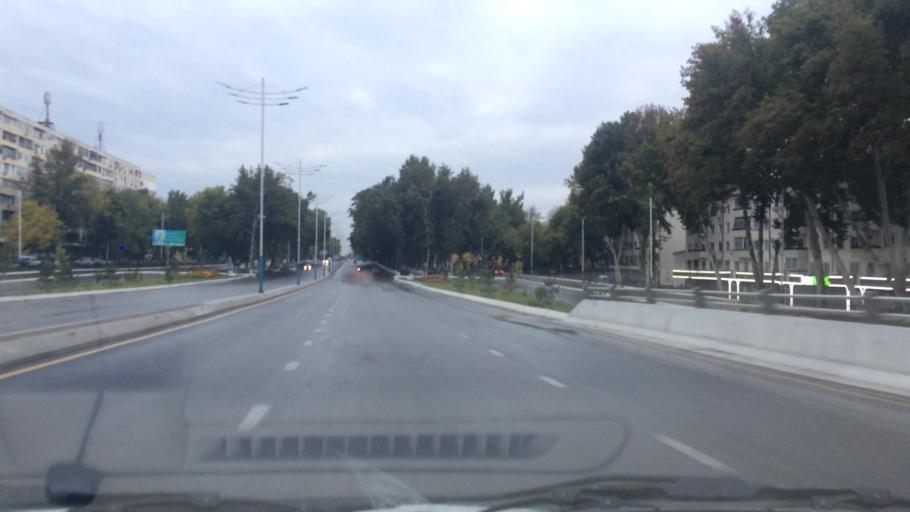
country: UZ
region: Toshkent Shahri
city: Tashkent
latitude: 41.2902
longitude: 69.2213
